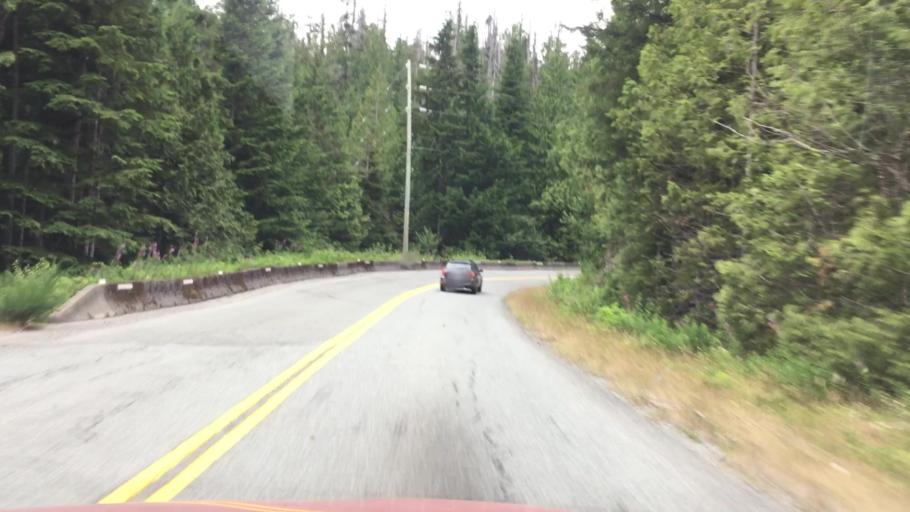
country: CA
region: British Columbia
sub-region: Regional District of Alberni-Clayoquot
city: Ucluelet
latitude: 49.1059
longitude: -125.4564
